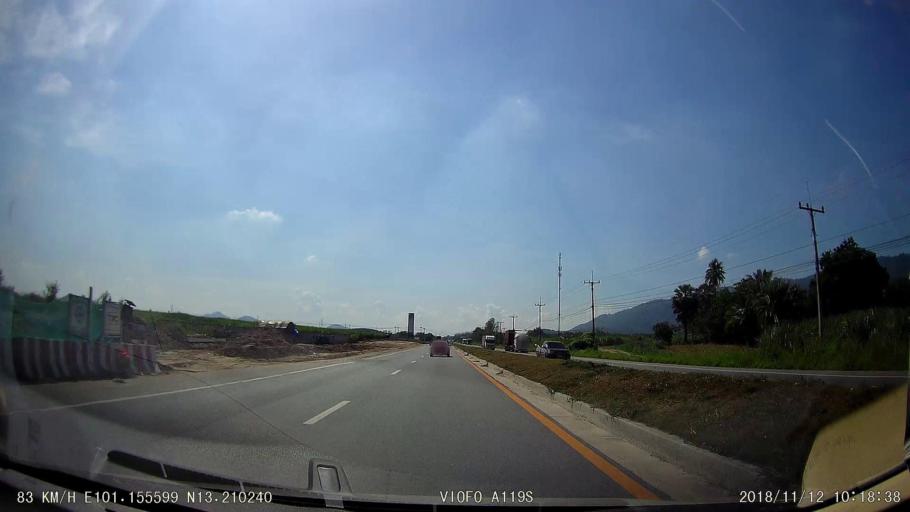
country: TH
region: Chon Buri
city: Ban Bueng
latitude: 13.2098
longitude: 101.1557
